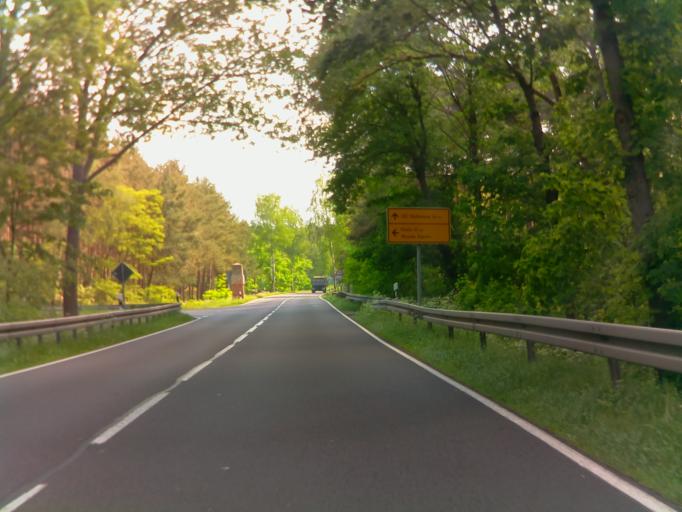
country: DE
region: Saxony-Anhalt
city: Schonhausen
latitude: 52.5701
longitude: 12.1526
